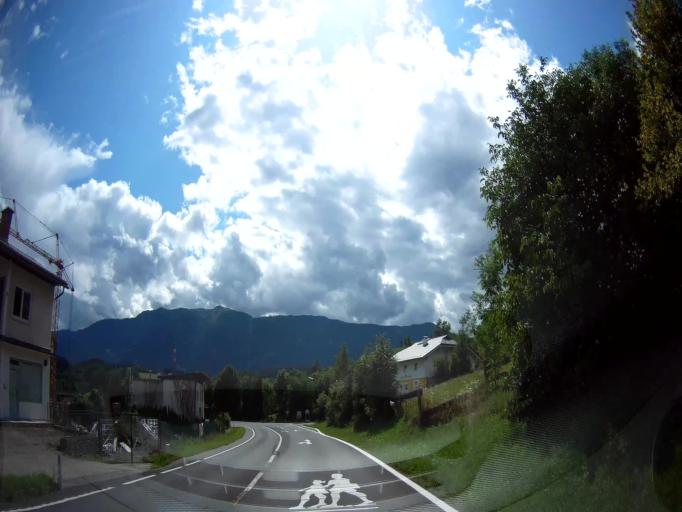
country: AT
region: Carinthia
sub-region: Politischer Bezirk Spittal an der Drau
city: Seeboden
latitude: 46.8288
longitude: 13.4912
